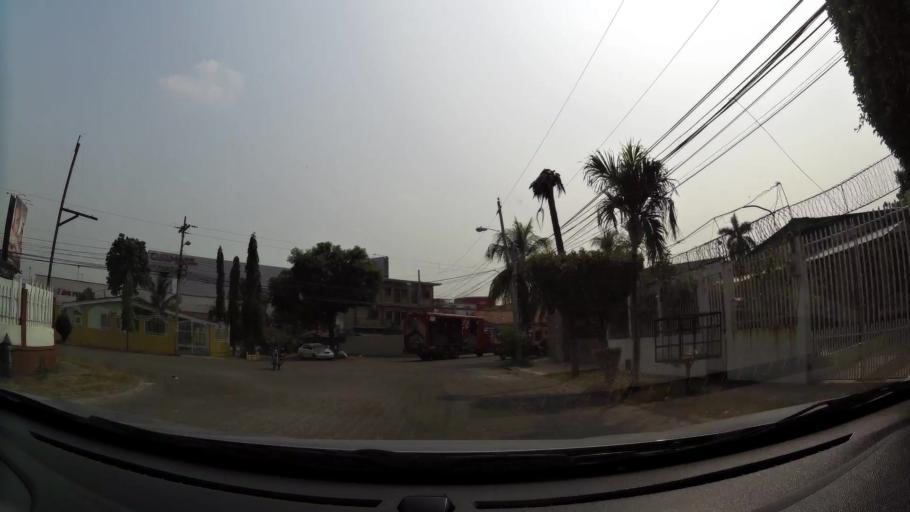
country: HN
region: Cortes
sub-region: San Pedro Sula
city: Pena Blanca
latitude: 15.5292
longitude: -88.0296
